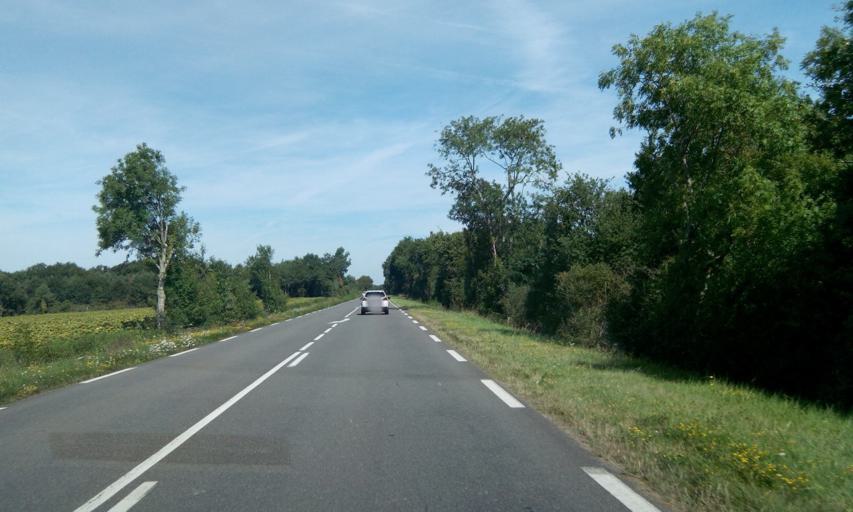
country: FR
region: Poitou-Charentes
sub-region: Departement de la Charente
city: Confolens
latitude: 46.0580
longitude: 0.6086
